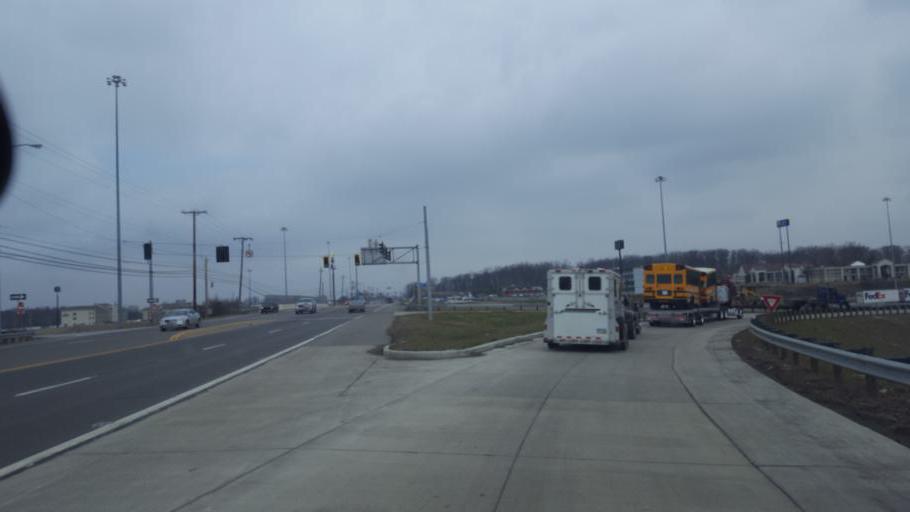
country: US
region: Ohio
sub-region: Trumbull County
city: Mineral Ridge
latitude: 41.1223
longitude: -80.7680
